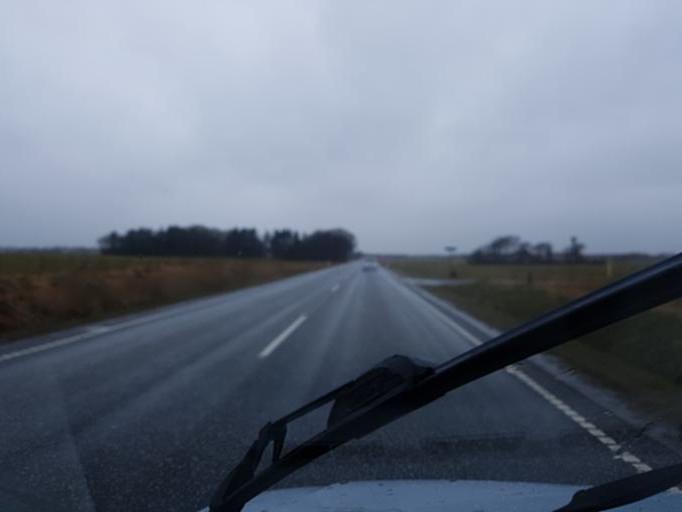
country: DK
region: Central Jutland
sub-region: Ringkobing-Skjern Kommune
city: Skjern
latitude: 56.0681
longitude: 8.5058
